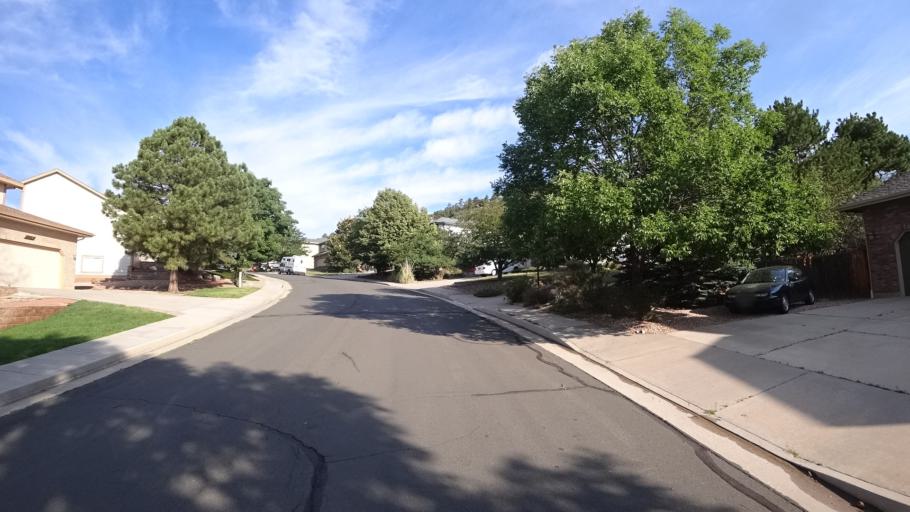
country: US
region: Colorado
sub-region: El Paso County
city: Air Force Academy
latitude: 38.9258
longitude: -104.8514
